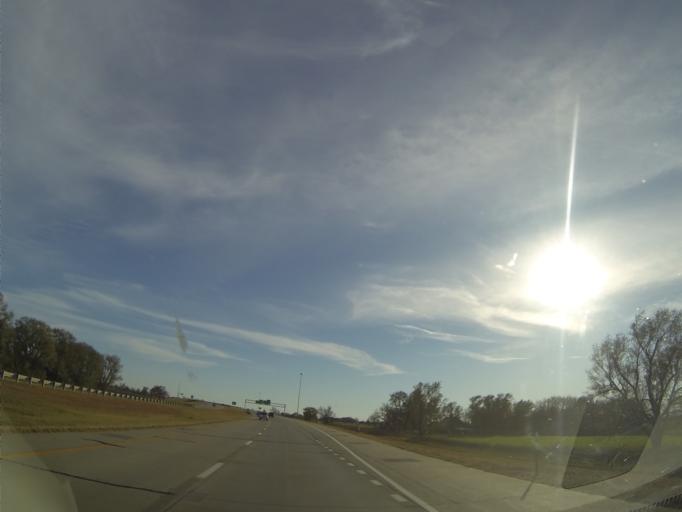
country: US
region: Kansas
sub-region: Saline County
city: Salina
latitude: 38.8465
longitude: -97.6479
